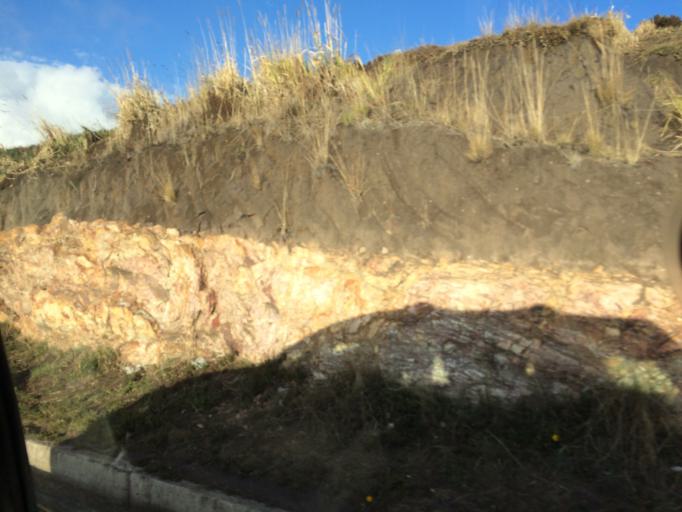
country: EC
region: Chimborazo
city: Alausi
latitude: -2.1389
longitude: -78.7189
